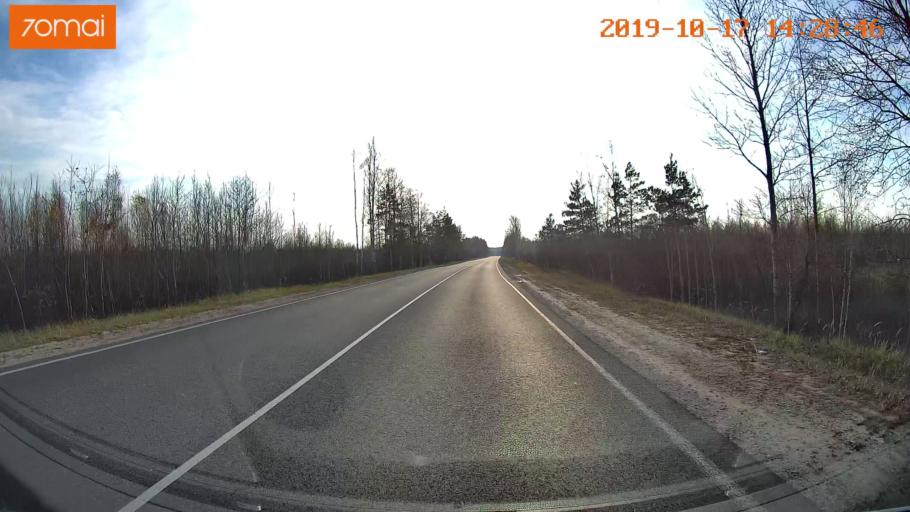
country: RU
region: Rjazan
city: Solotcha
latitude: 54.9688
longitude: 39.9505
